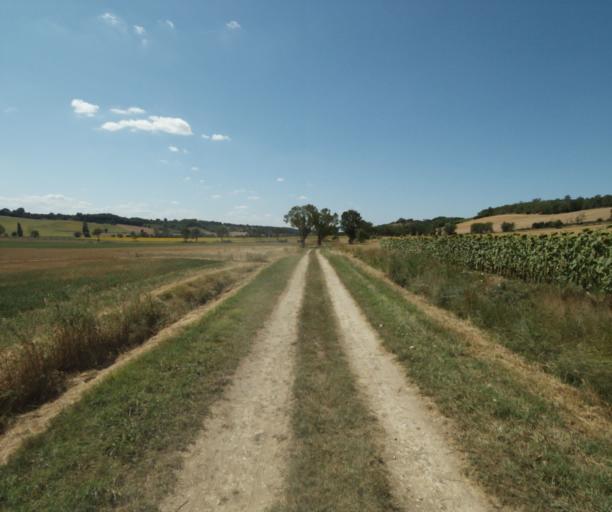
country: FR
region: Midi-Pyrenees
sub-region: Departement de la Haute-Garonne
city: Saint-Felix-Lauragais
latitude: 43.4951
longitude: 1.8771
